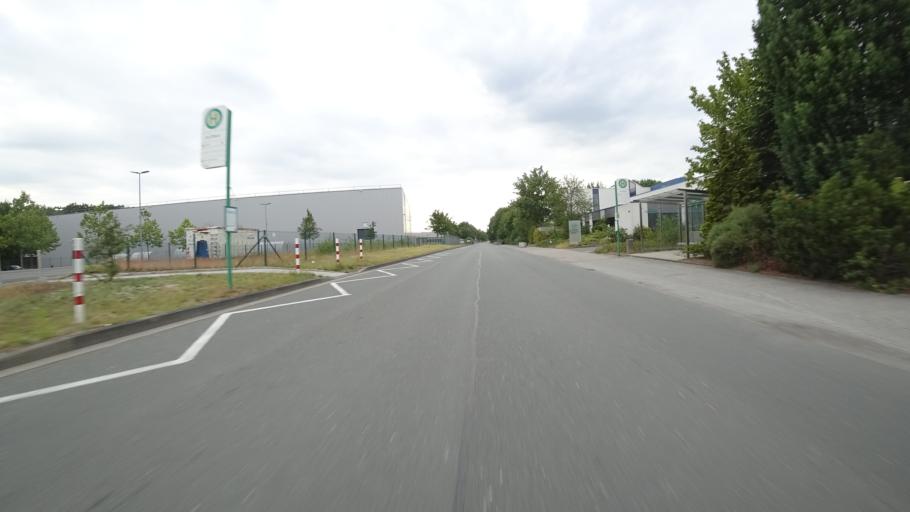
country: DE
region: North Rhine-Westphalia
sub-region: Regierungsbezirk Detmold
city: Verl
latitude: 51.8849
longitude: 8.4487
